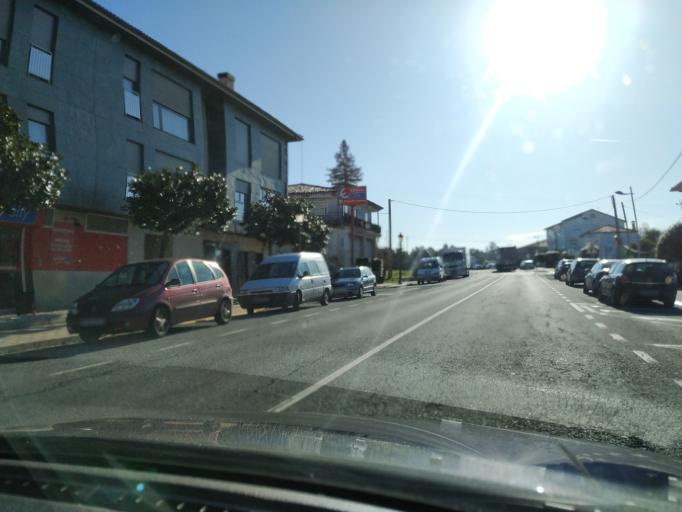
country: ES
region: Galicia
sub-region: Provincia da Coruna
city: Vedra
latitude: 42.7970
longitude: -8.4691
